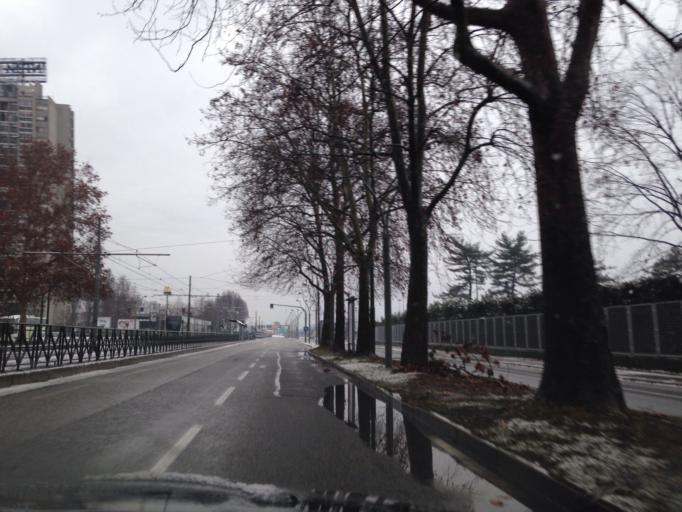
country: IT
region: Piedmont
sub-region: Provincia di Torino
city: Turin
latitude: 45.1149
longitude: 7.7087
